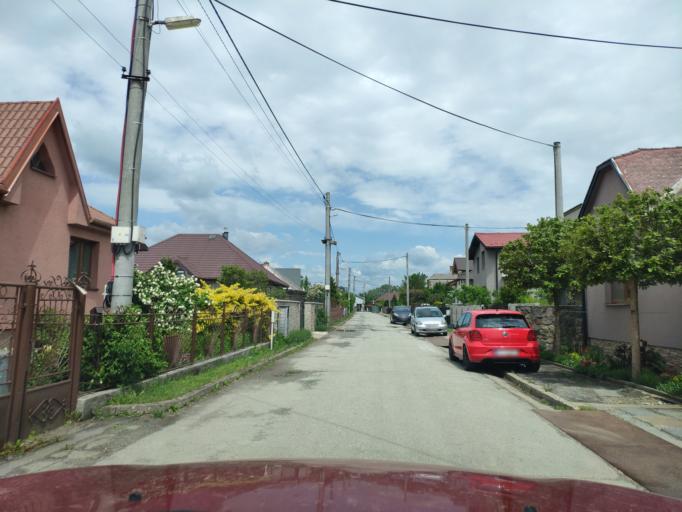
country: SK
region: Kosicky
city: Kosice
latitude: 48.7297
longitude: 21.3392
